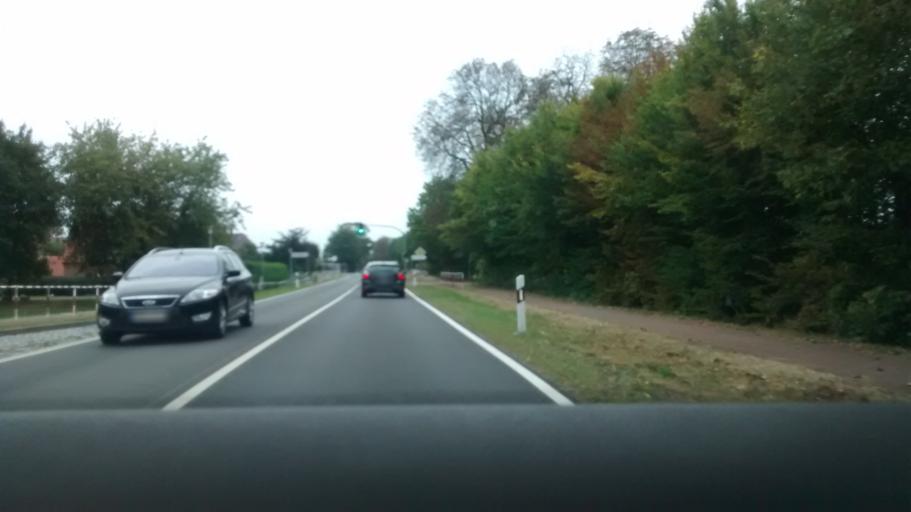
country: DE
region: Mecklenburg-Vorpommern
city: Mecklenburg
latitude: 53.8165
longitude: 11.4466
